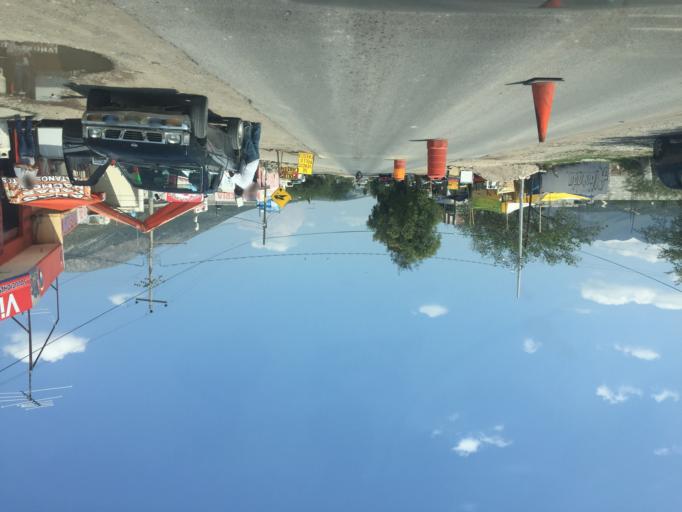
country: MX
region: Hidalgo
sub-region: Ixmiquilpan
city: El Nith
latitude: 20.5801
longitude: -99.1346
